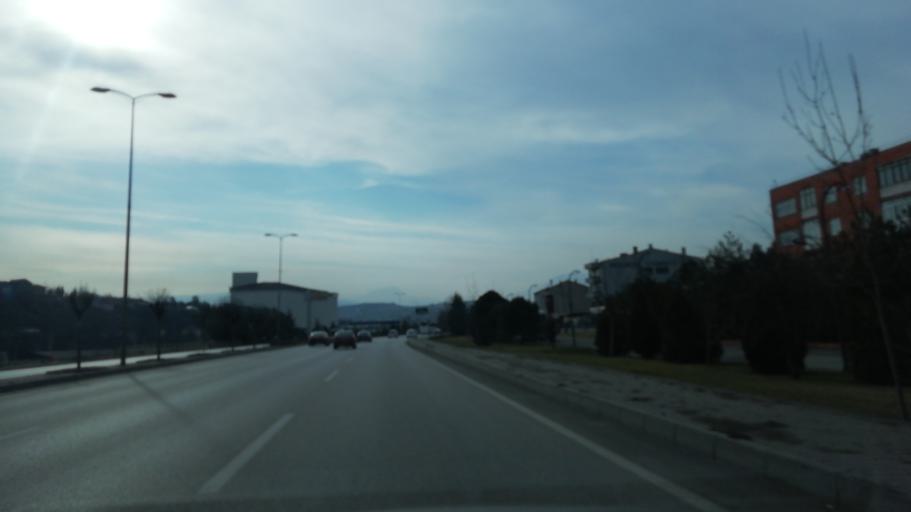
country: TR
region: Karabuk
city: Karabuk
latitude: 41.2011
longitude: 32.6293
